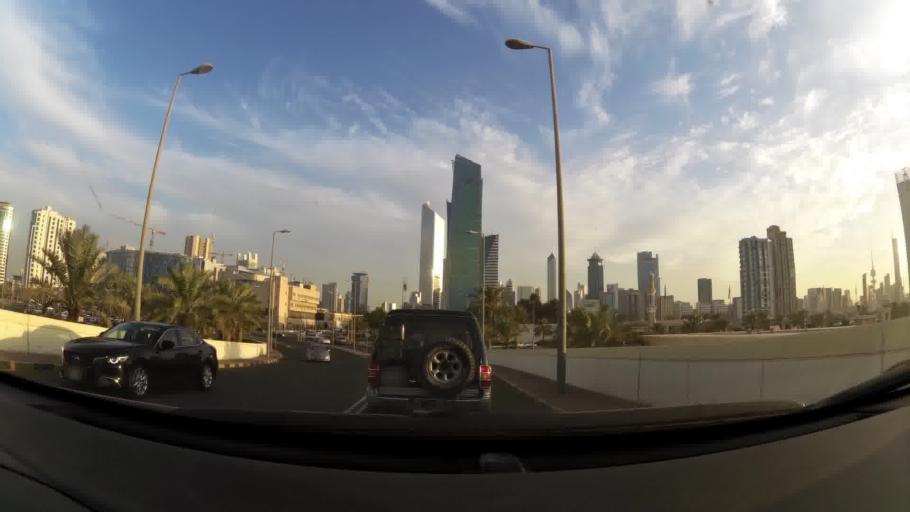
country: KW
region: Al Asimah
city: Kuwait City
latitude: 29.3893
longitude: 47.9840
